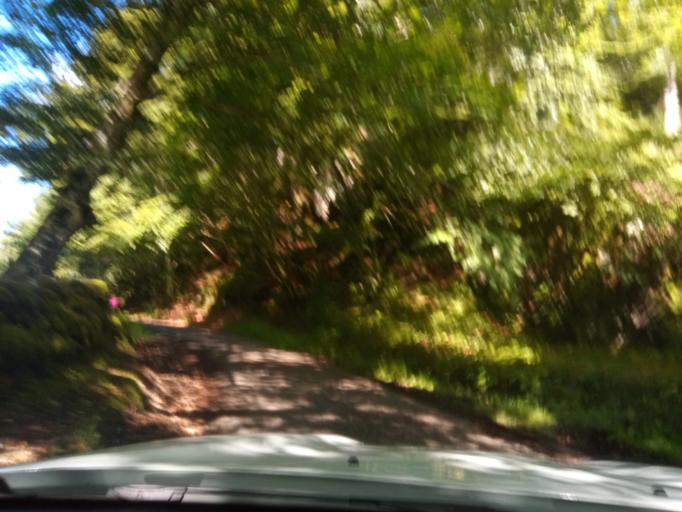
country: GB
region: Scotland
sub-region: Argyll and Bute
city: Isle Of Mull
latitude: 56.7576
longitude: -5.8085
